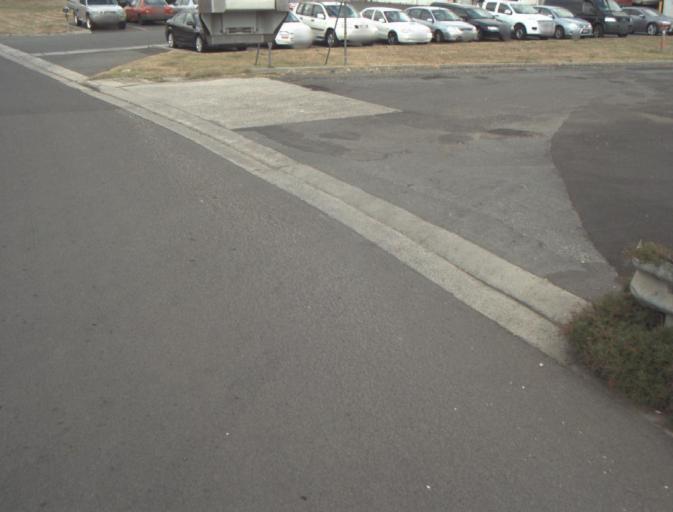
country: AU
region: Tasmania
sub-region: Launceston
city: Summerhill
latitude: -41.4755
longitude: 147.1636
